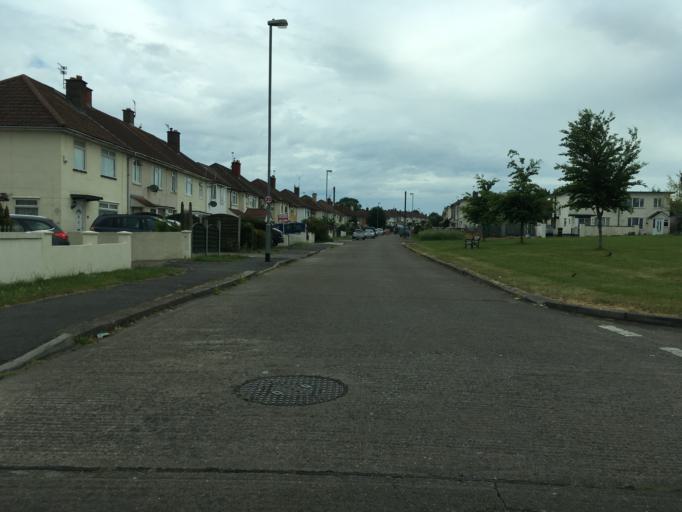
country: GB
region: England
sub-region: South Gloucestershire
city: Stoke Gifford
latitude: 51.4911
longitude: -2.5677
